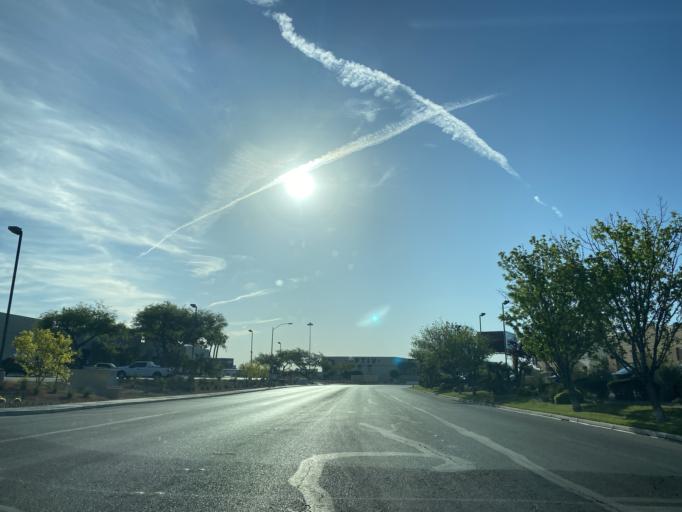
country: US
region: Nevada
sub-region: Clark County
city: Paradise
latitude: 36.0679
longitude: -115.1500
